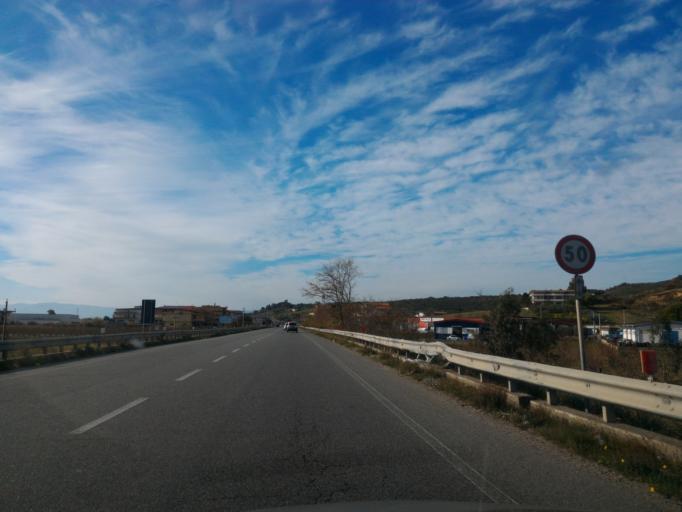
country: IT
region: Calabria
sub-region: Provincia di Catanzaro
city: Sellia Marina
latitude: 38.8959
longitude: 16.7297
